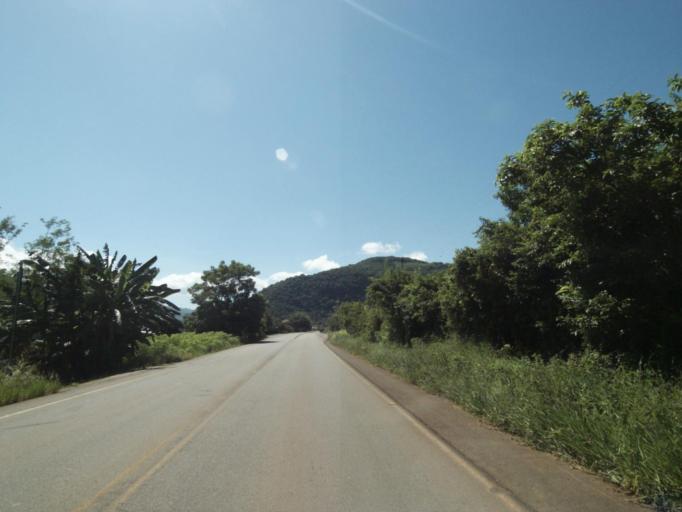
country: BR
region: Rio Grande do Sul
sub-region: Bento Goncalves
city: Bento Goncalves
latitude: -29.0924
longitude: -51.6302
